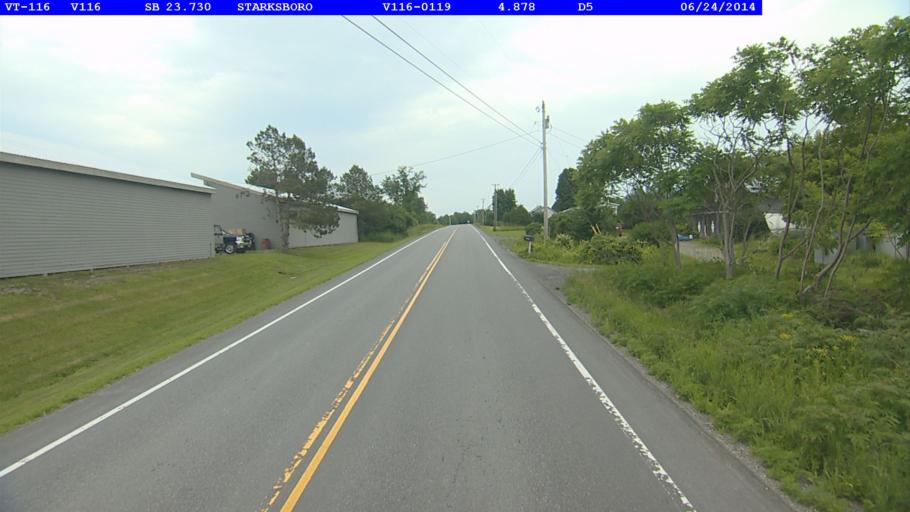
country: US
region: Vermont
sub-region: Chittenden County
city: Hinesburg
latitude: 44.2545
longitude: -73.0633
